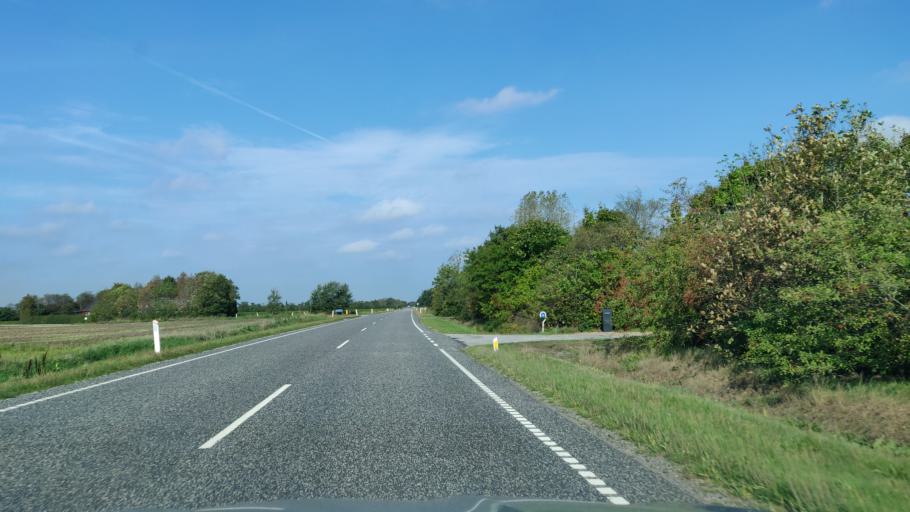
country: DK
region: Central Jutland
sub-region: Herning Kommune
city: Sunds
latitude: 56.2490
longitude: 9.0620
